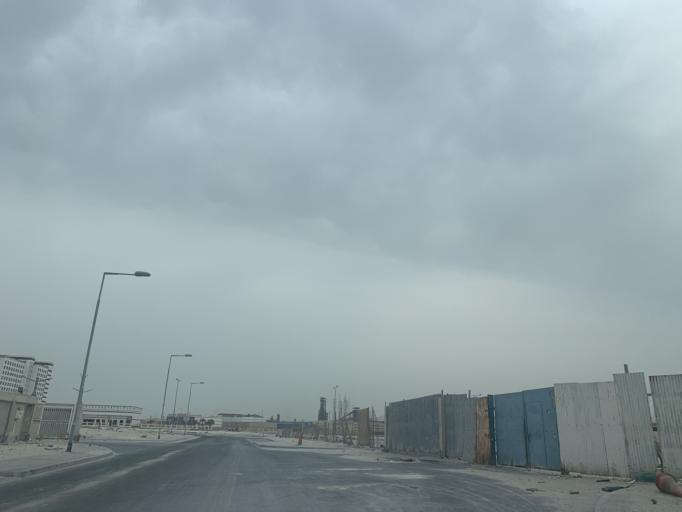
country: BH
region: Muharraq
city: Al Hadd
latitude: 26.2144
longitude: 50.6823
